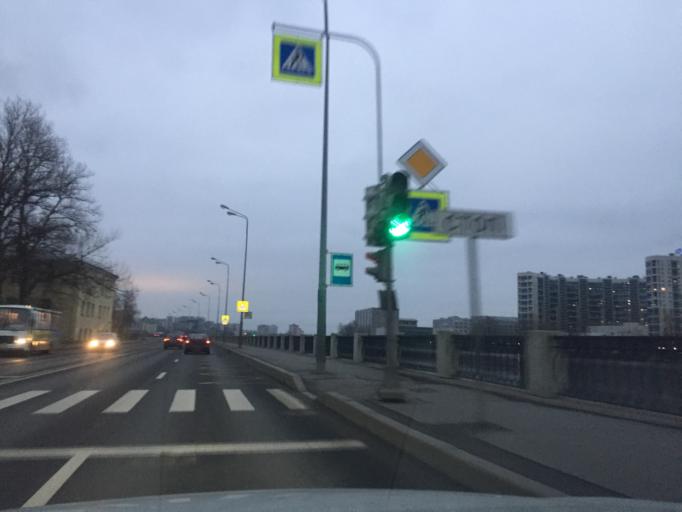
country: RU
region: St.-Petersburg
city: Obukhovo
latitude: 59.8718
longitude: 30.4647
